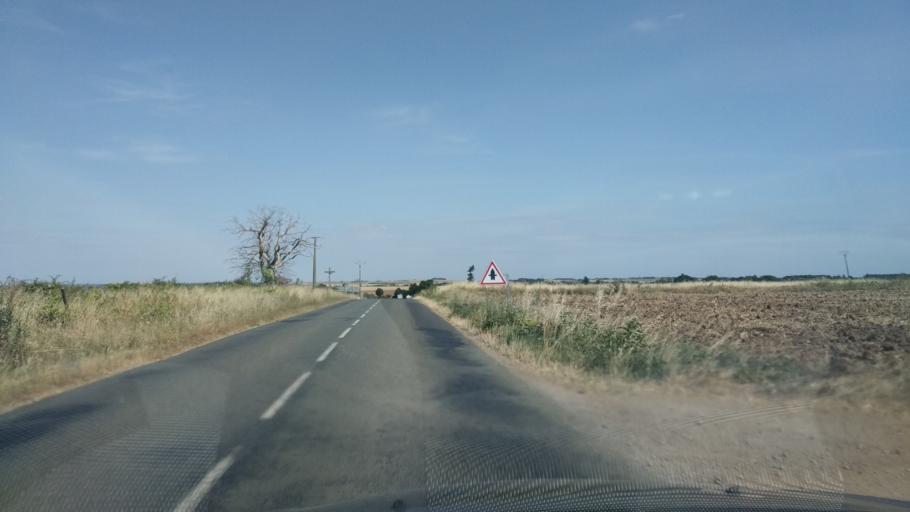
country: FR
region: Poitou-Charentes
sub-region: Departement de la Vienne
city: Vouille
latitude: 46.6827
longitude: 0.1685
